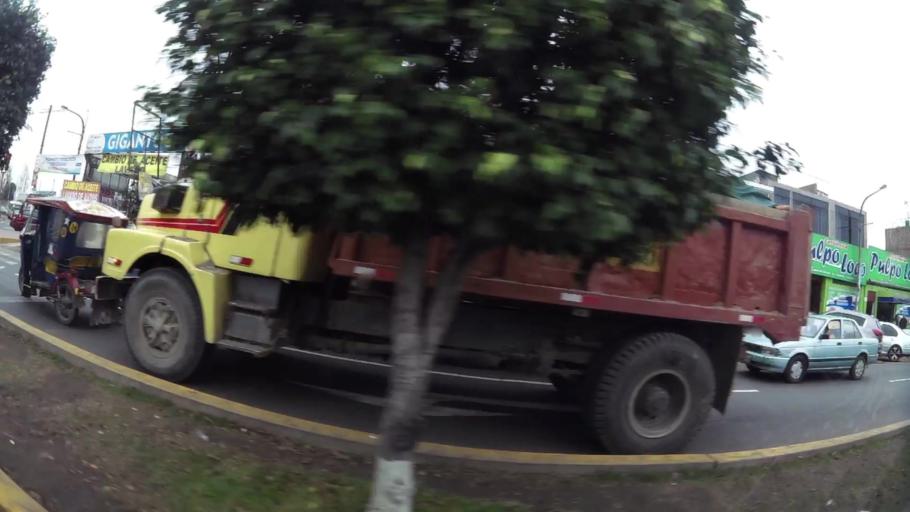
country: PE
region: Lima
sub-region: Lima
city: Vitarte
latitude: -12.0438
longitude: -76.9703
